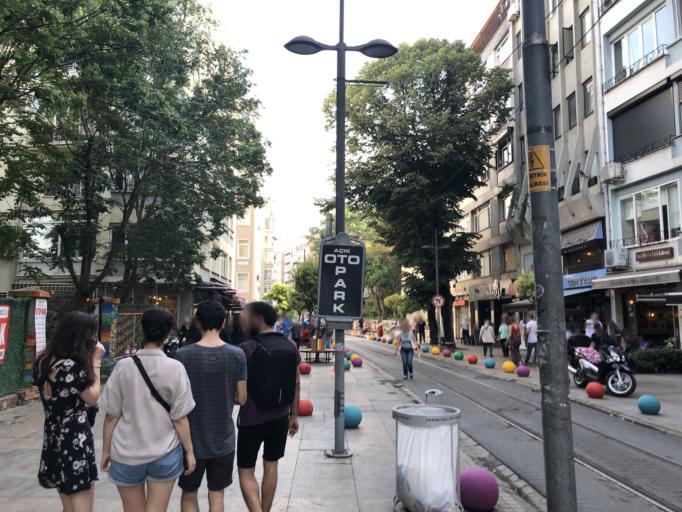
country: TR
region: Istanbul
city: UEskuedar
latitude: 40.9866
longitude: 29.0282
